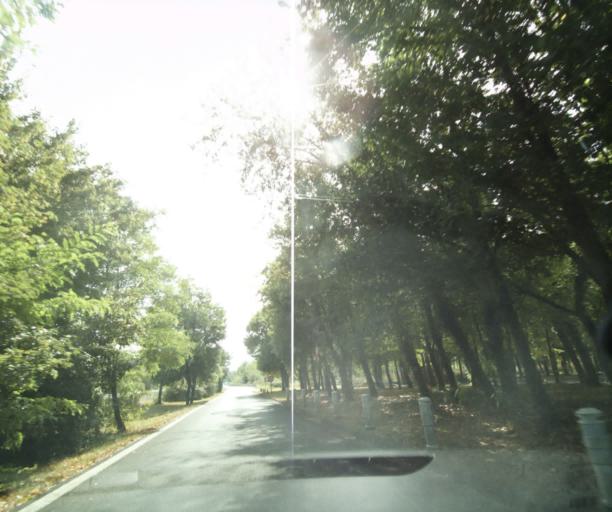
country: FR
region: Poitou-Charentes
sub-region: Departement de la Charente-Maritime
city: Pons
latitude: 45.6093
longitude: -0.5986
